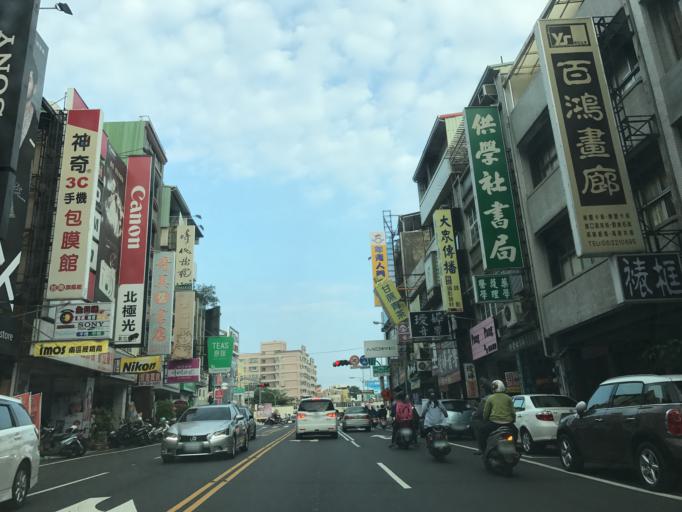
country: TW
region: Taiwan
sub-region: Tainan
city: Tainan
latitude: 22.9945
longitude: 120.2111
